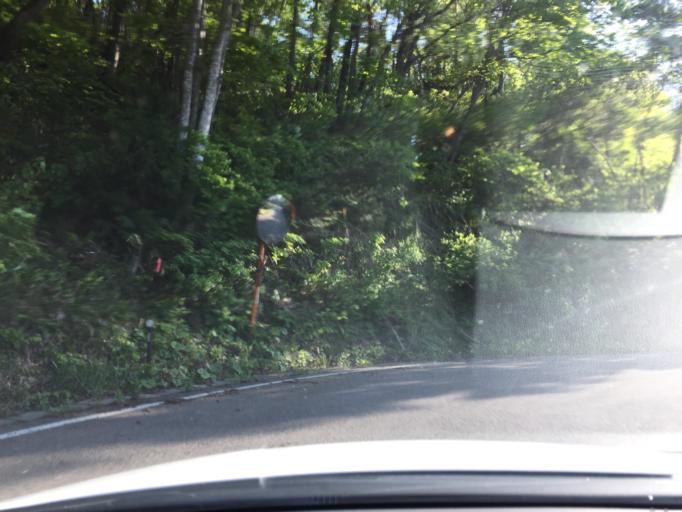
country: JP
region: Fukushima
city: Kitakata
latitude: 37.6721
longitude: 139.8050
